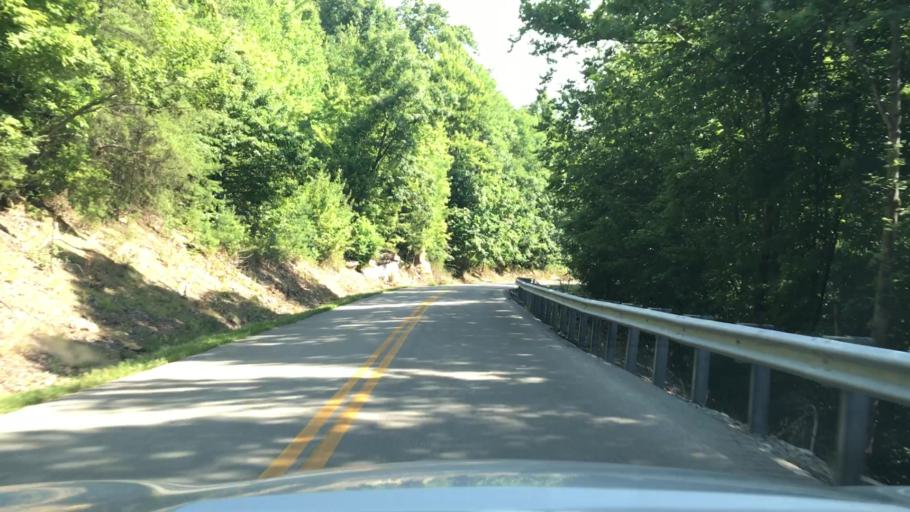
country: US
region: Kentucky
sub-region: Clinton County
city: Albany
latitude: 36.7212
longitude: -85.0207
